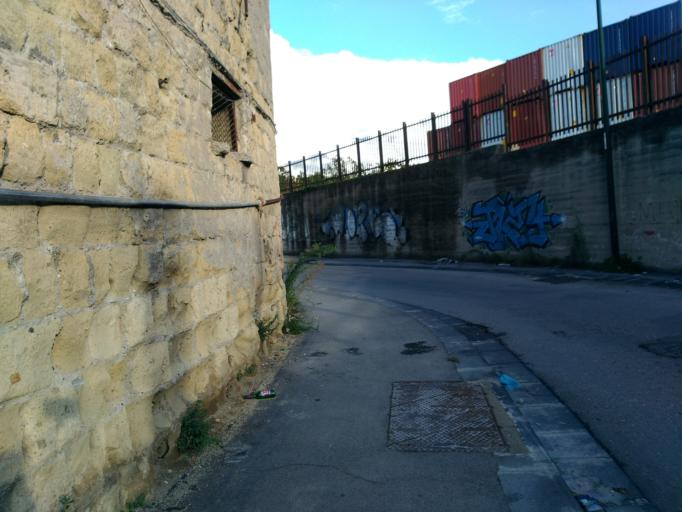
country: IT
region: Campania
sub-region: Provincia di Napoli
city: Napoli
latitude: 40.8449
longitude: 14.2880
